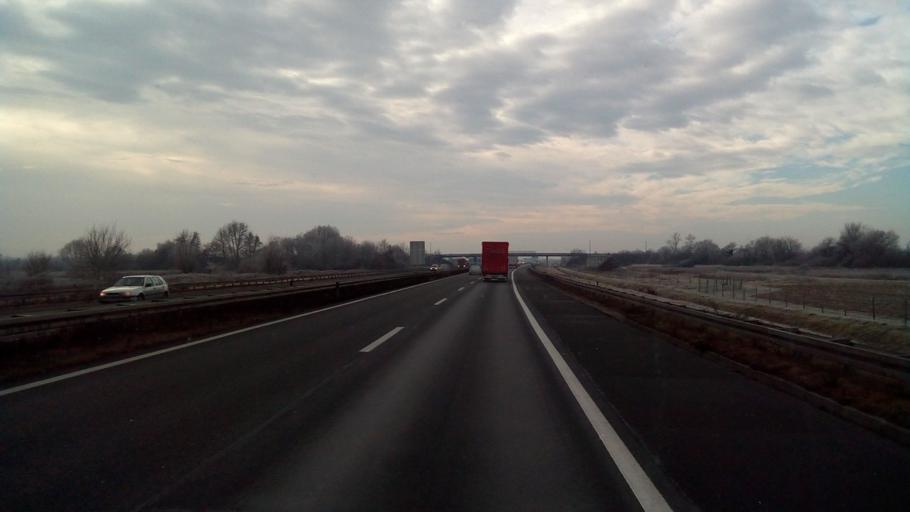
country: HR
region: Grad Zagreb
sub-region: Sesvete
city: Sesvete
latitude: 45.7802
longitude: 16.1147
